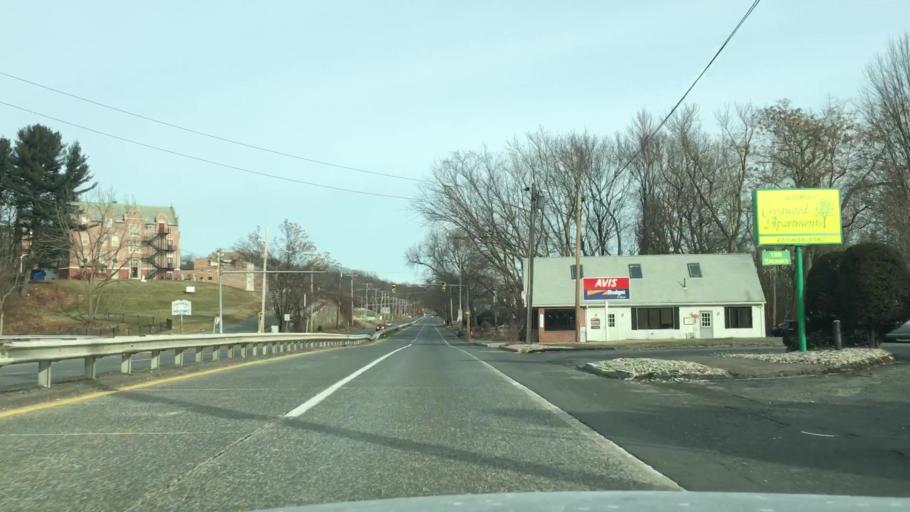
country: US
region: Massachusetts
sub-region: Hampden County
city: Chicopee
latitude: 42.1616
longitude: -72.6331
